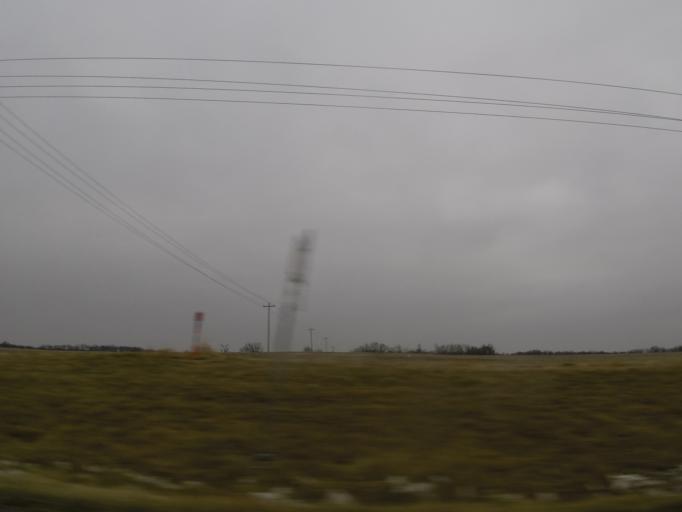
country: US
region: Missouri
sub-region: Marion County
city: Palmyra
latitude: 39.7436
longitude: -91.4807
